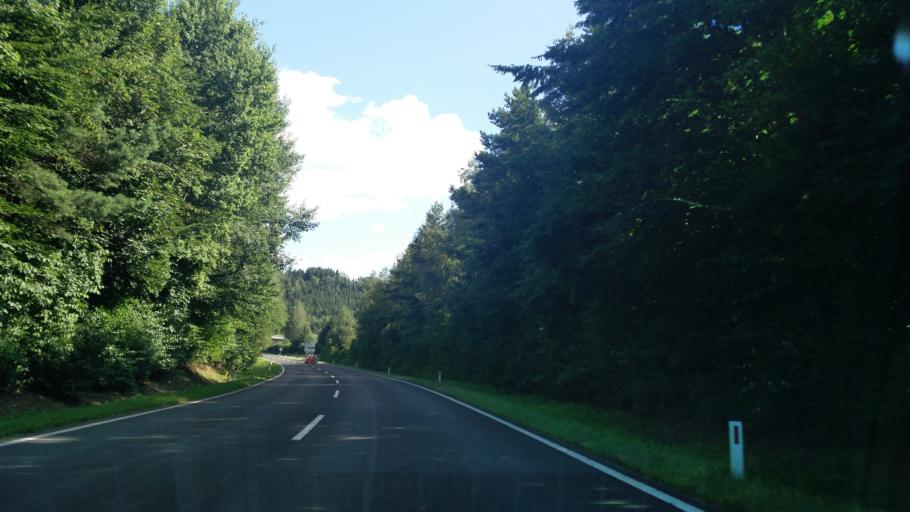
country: AT
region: Styria
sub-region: Politischer Bezirk Leoben
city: Trofaiach
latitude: 47.4237
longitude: 14.9997
